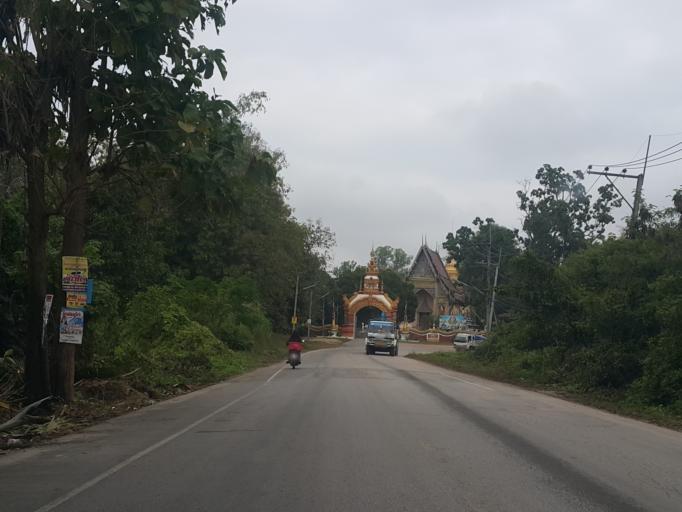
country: TH
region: Lampang
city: Lampang
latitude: 18.3116
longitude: 99.4948
